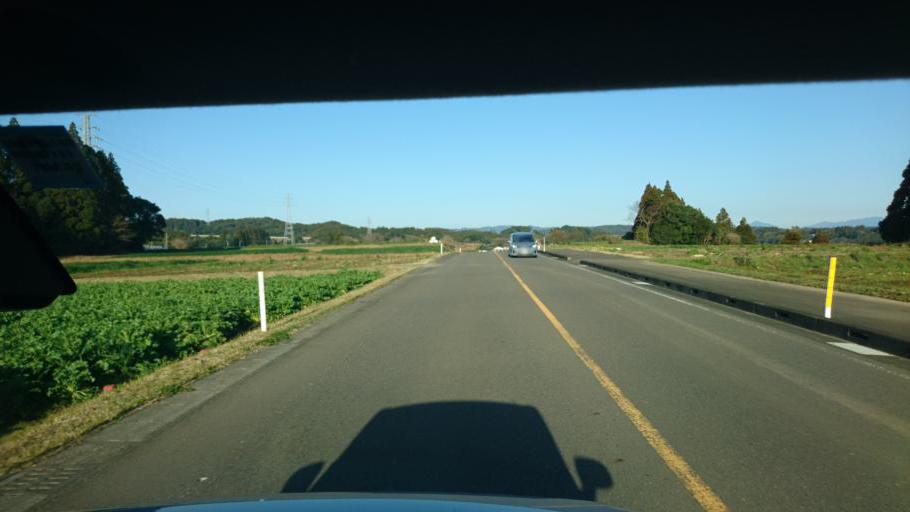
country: JP
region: Miyazaki
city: Miyazaki-shi
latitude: 31.8502
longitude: 131.3802
